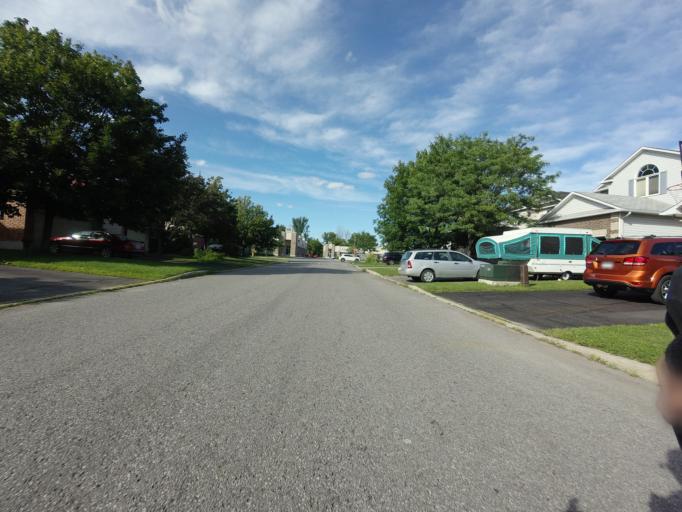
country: CA
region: Ontario
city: Ottawa
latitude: 45.2822
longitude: -75.6869
